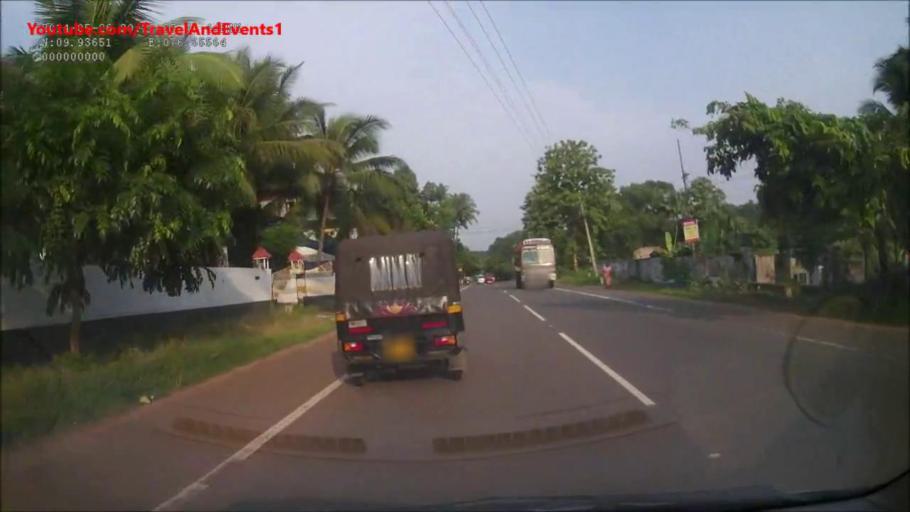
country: IN
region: Kerala
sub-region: Ernakulam
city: Muvattupula
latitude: 9.9326
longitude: 76.6620
